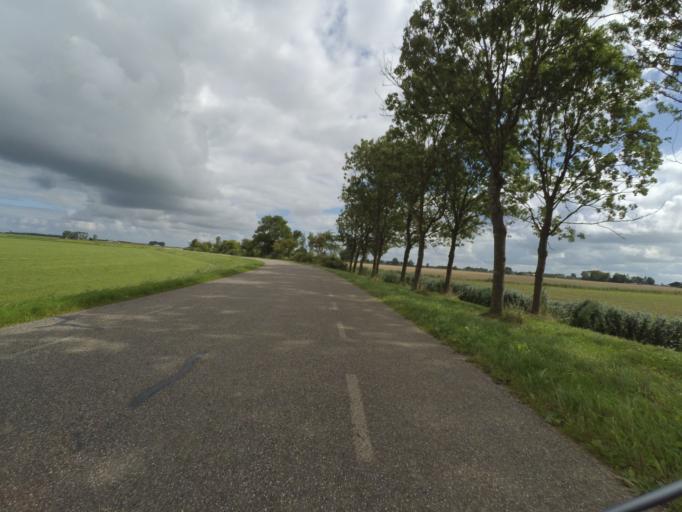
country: NL
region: Groningen
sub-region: Gemeente Zuidhorn
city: Grijpskerk
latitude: 53.3017
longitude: 6.2506
